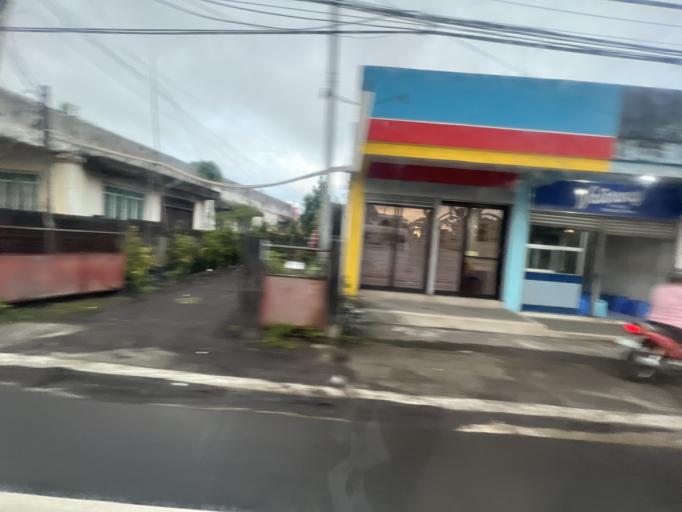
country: PH
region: Bicol
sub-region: Province of Albay
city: Sagpon
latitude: 13.1532
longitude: 123.7345
